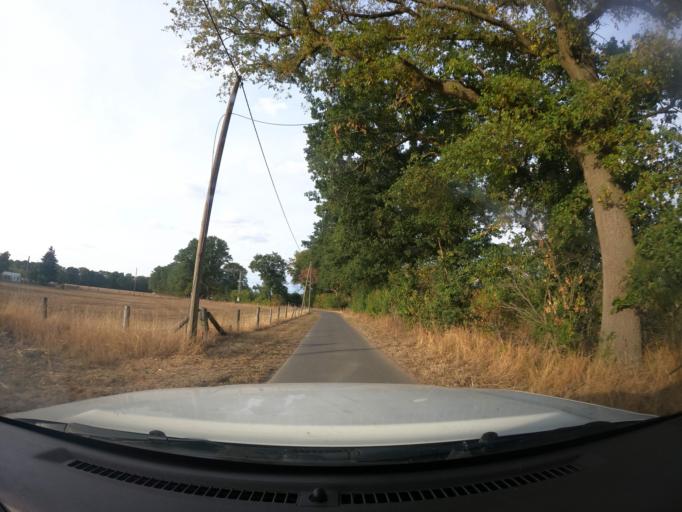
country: DE
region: North Rhine-Westphalia
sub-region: Regierungsbezirk Dusseldorf
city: Hamminkeln
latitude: 51.7034
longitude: 6.5737
